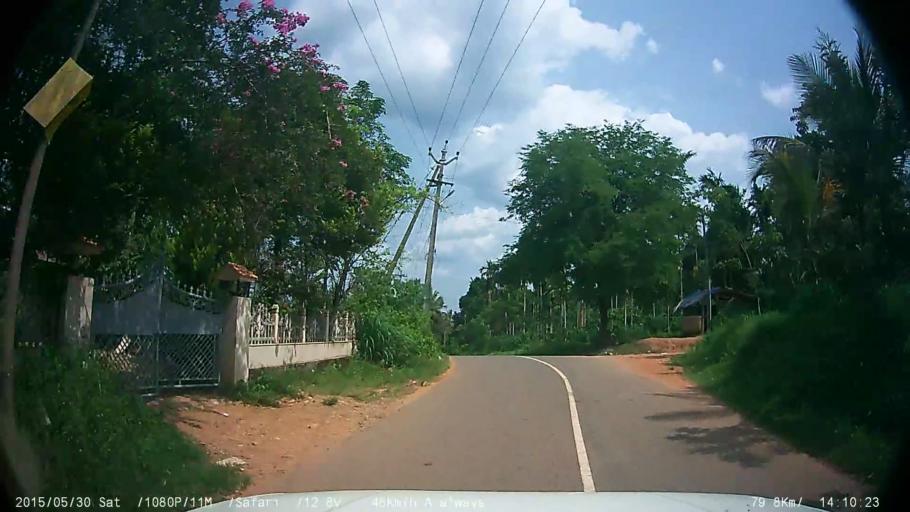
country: IN
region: Kerala
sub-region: Wayanad
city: Panamaram
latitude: 11.7997
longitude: 76.0526
